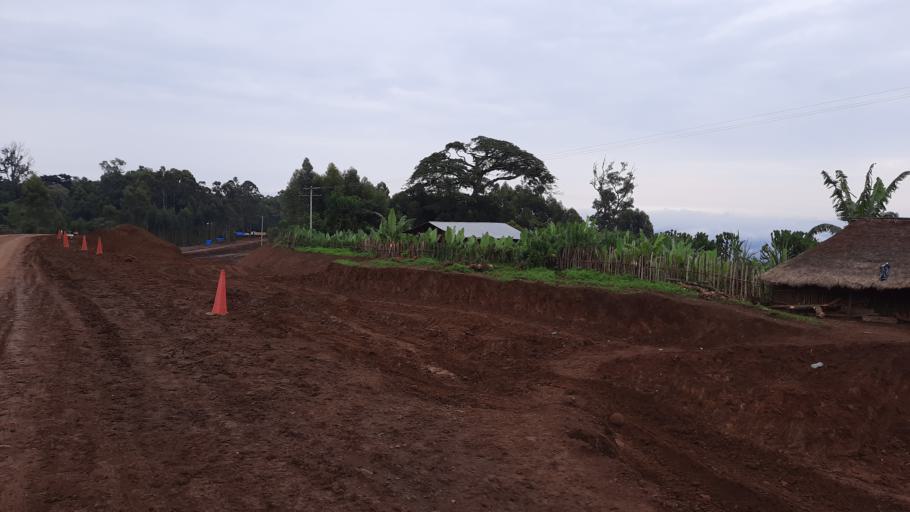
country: ET
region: Oromiya
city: Gore
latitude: 7.8138
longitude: 35.4587
